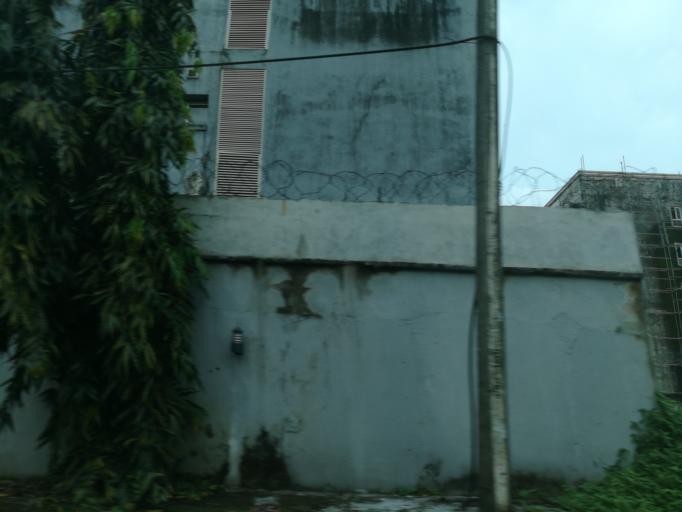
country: NG
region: Rivers
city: Port Harcourt
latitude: 4.8182
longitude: 6.9941
